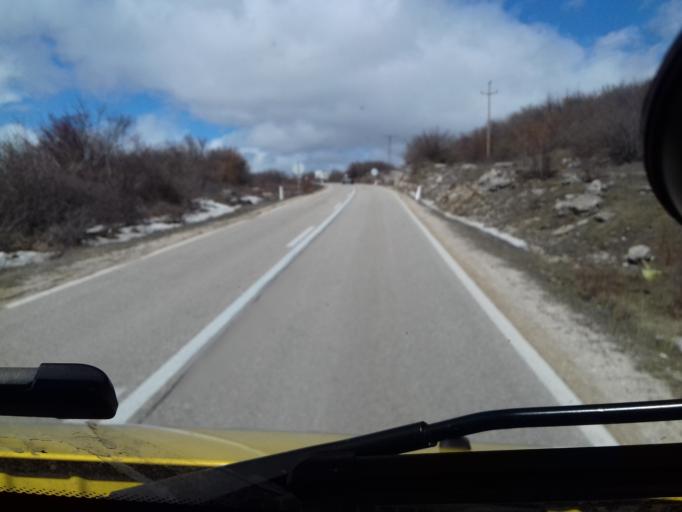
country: BA
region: Federation of Bosnia and Herzegovina
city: Tomislavgrad
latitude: 43.7780
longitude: 17.2269
